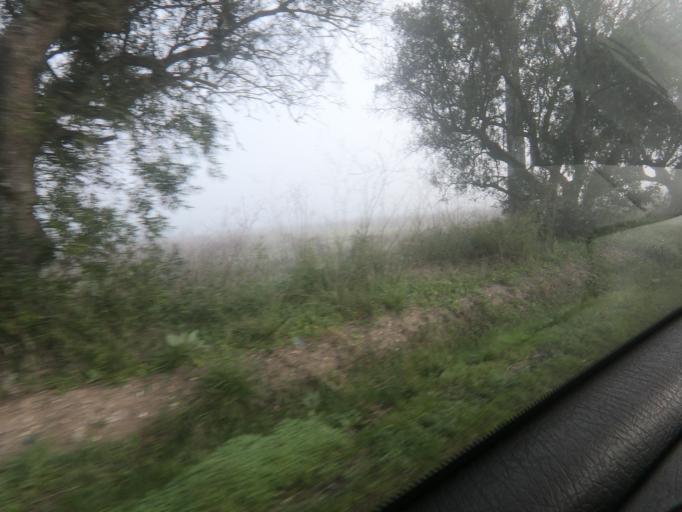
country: PT
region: Setubal
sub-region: Palmela
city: Palmela
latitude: 38.6070
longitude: -8.8506
